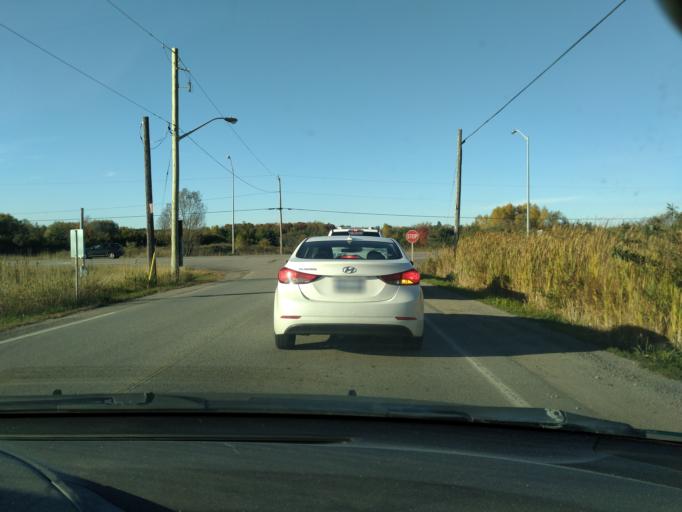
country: CA
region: Ontario
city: Bradford West Gwillimbury
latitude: 43.9997
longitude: -79.7276
